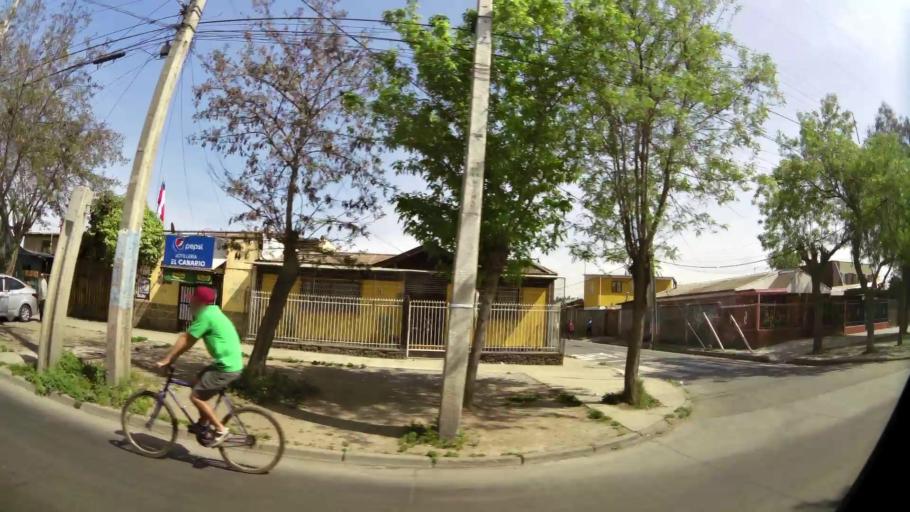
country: CL
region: Santiago Metropolitan
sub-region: Provincia de Santiago
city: Lo Prado
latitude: -33.4315
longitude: -70.7624
